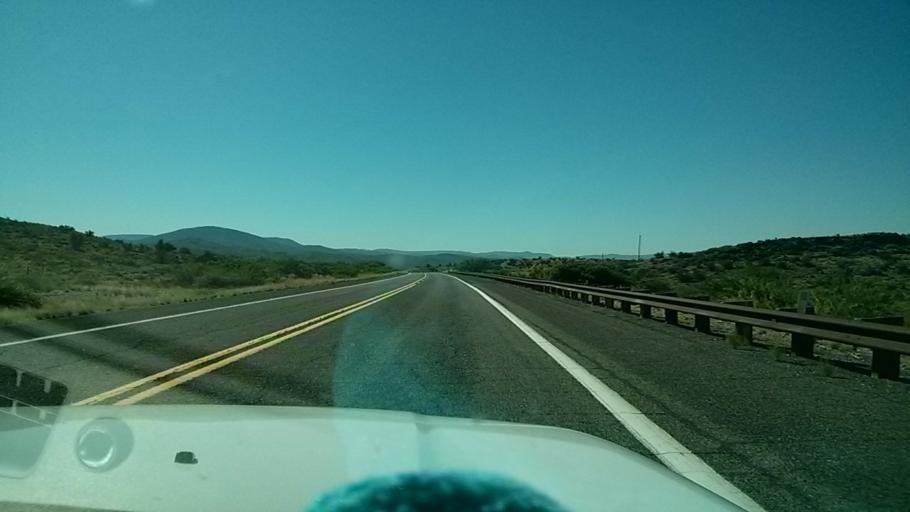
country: US
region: Arizona
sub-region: Mohave County
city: Peach Springs
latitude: 35.3699
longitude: -113.7164
